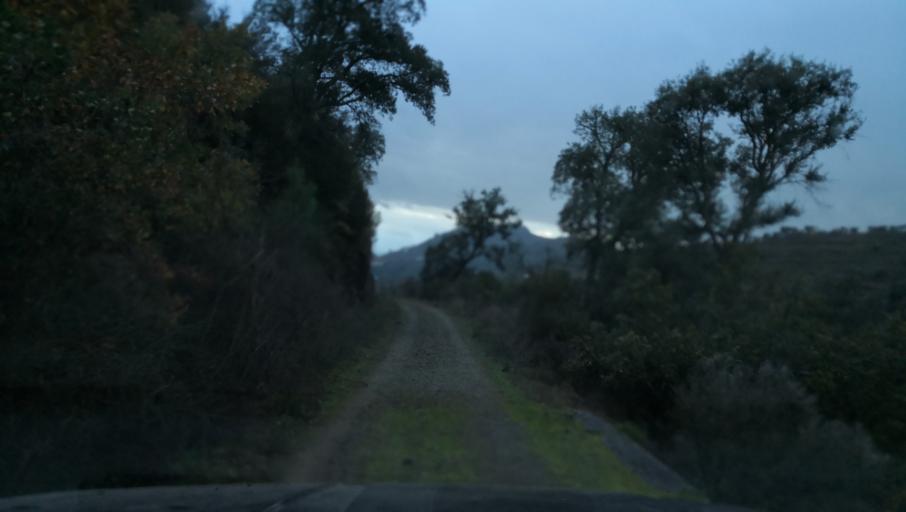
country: PT
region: Vila Real
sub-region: Santa Marta de Penaguiao
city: Santa Marta de Penaguiao
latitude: 41.2111
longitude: -7.7612
